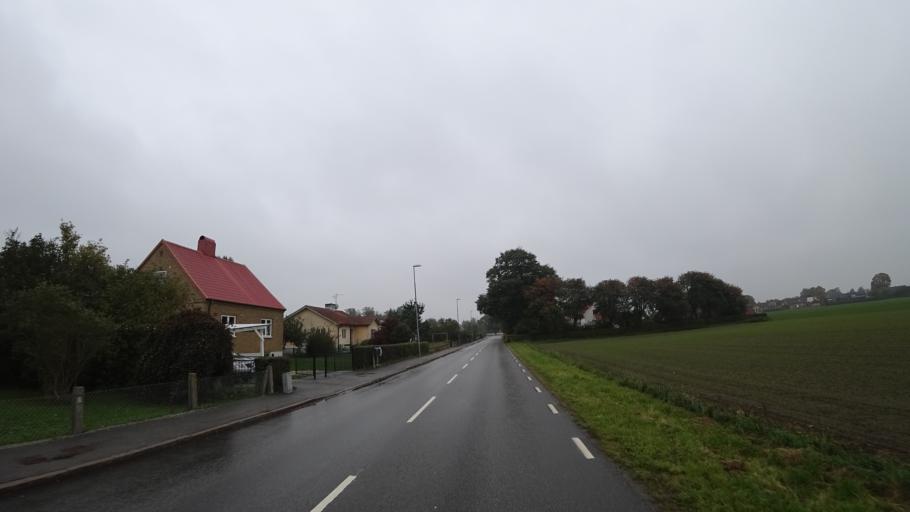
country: SE
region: Skane
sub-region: Kavlinge Kommun
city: Kaevlinge
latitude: 55.8069
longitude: 13.1569
